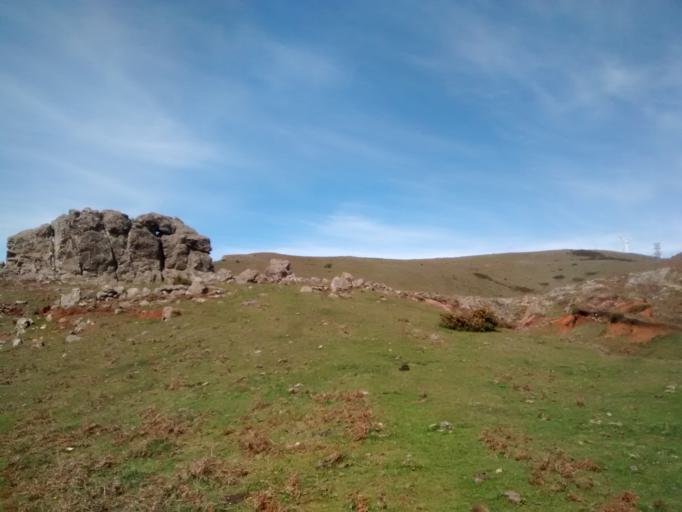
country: PT
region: Madeira
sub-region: Sao Vicente
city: Sao Vicente
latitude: 32.7321
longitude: -17.0629
